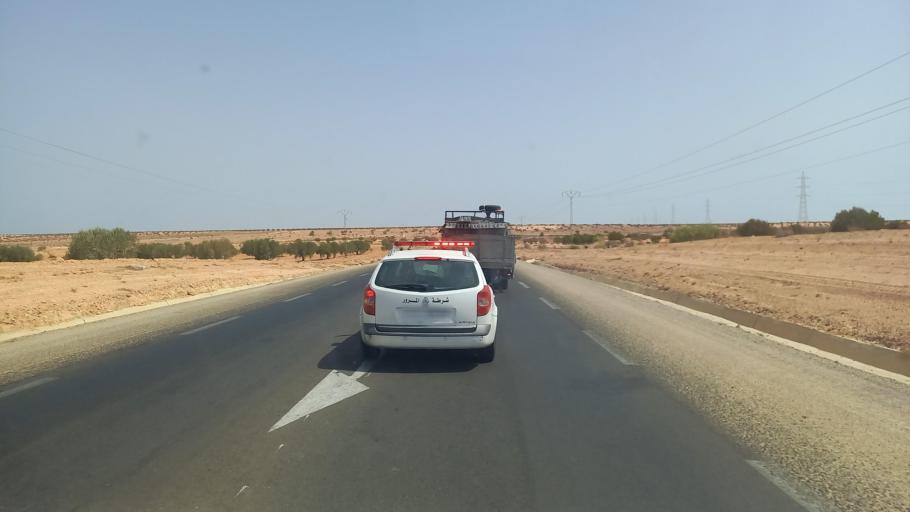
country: TN
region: Madanin
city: Zarzis
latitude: 33.4077
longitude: 10.8609
